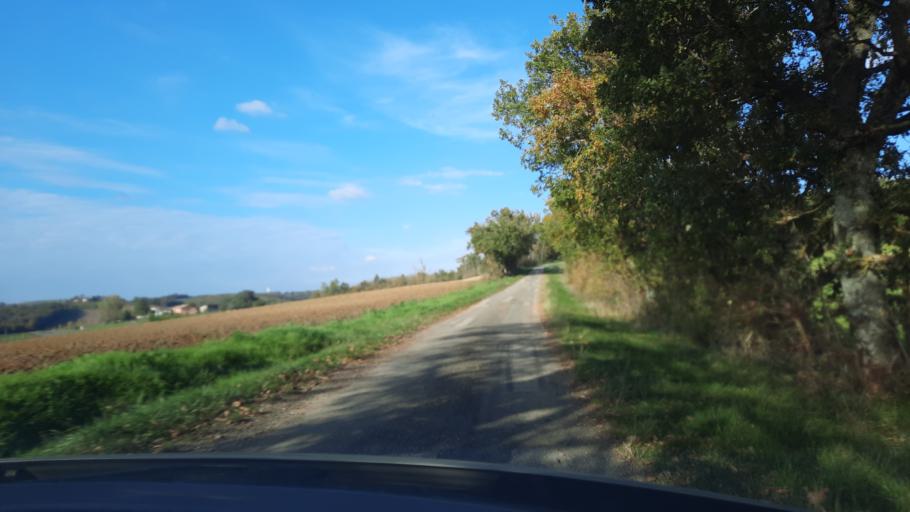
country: FR
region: Midi-Pyrenees
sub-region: Departement du Tarn-et-Garonne
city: Lafrancaise
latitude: 44.1750
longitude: 1.2822
